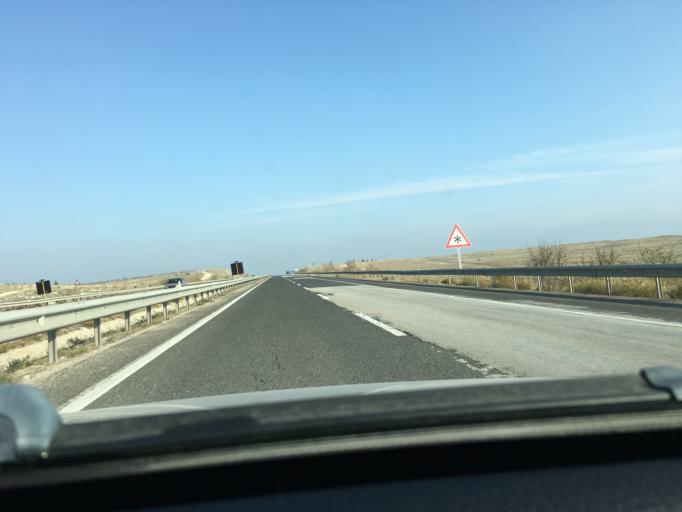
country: TR
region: Eskisehir
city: Gunyuzu
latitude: 39.5750
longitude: 31.8902
